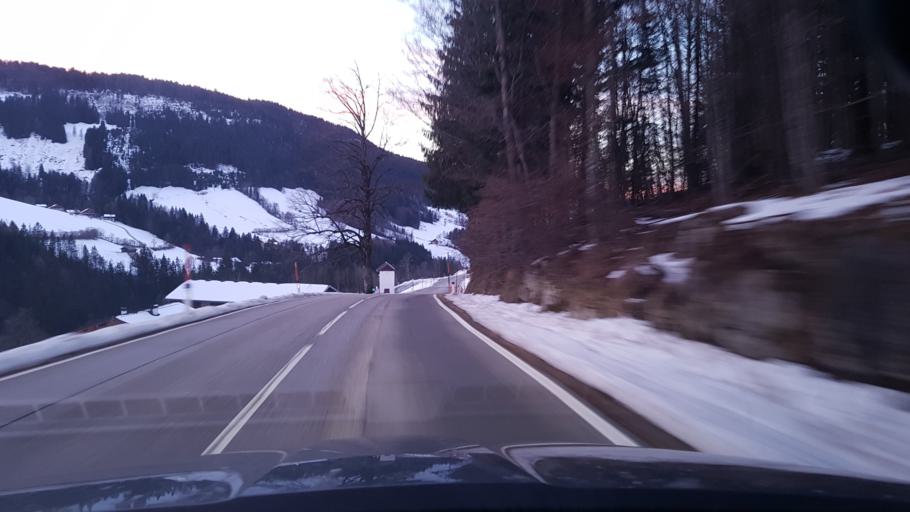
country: AT
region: Salzburg
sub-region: Politischer Bezirk Hallein
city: Krispl
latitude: 47.7024
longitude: 13.2125
